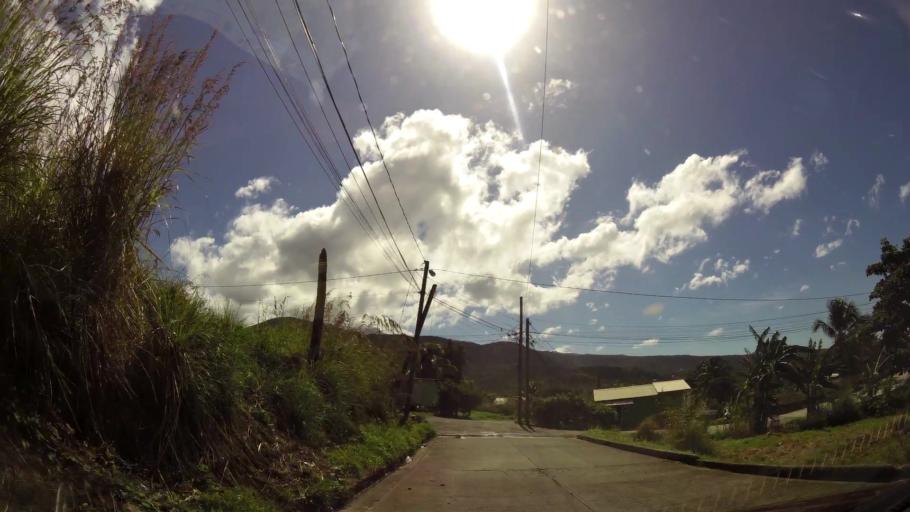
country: DM
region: Saint John
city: Portsmouth
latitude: 15.5786
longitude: -61.4512
